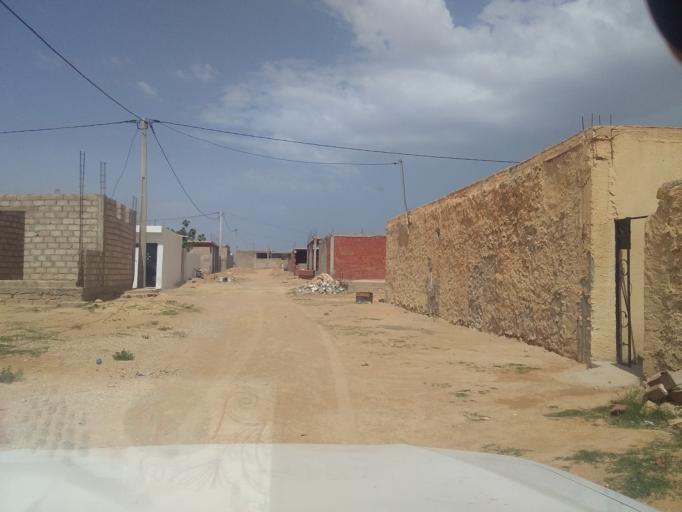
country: TN
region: Madanin
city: Medenine
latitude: 33.5877
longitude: 10.3268
